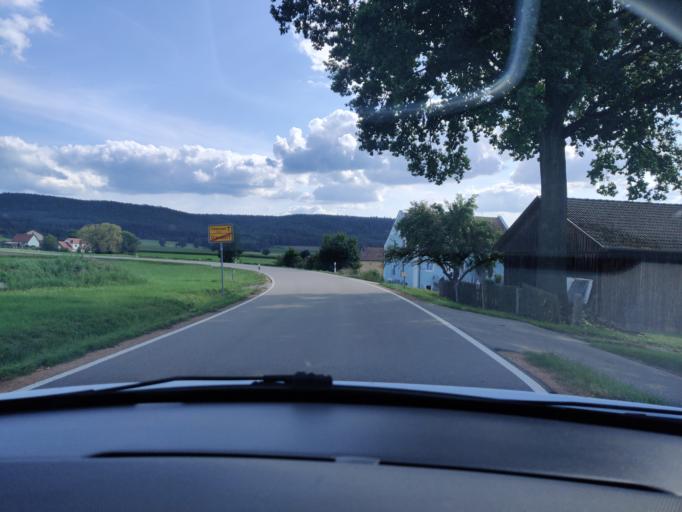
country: DE
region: Bavaria
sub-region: Upper Palatinate
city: Nabburg
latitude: 49.4411
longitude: 12.1909
